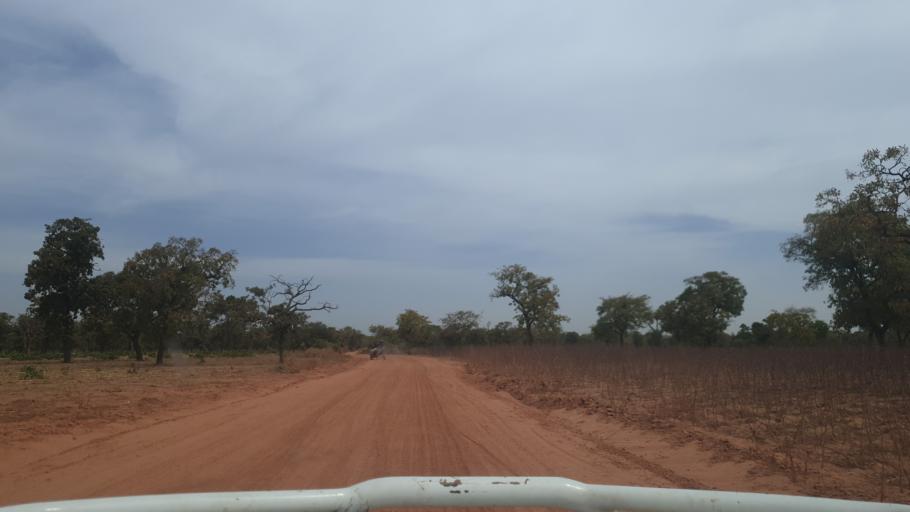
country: ML
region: Sikasso
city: Yorosso
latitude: 12.2229
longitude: -4.7529
